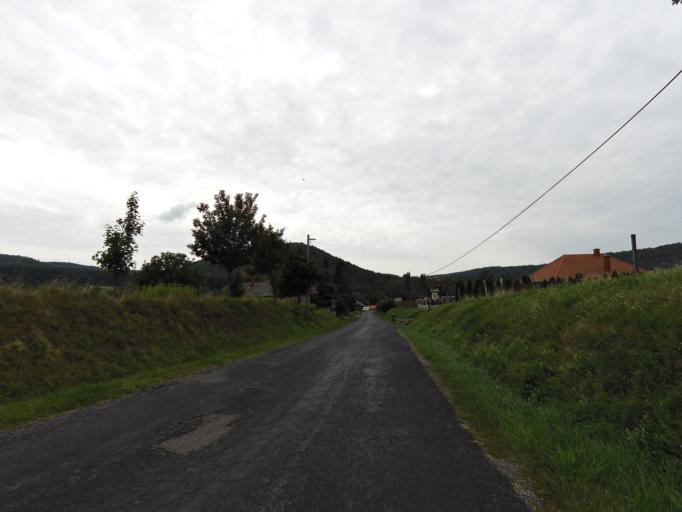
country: HU
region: Zala
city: Gyenesdias
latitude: 46.8488
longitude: 17.3034
